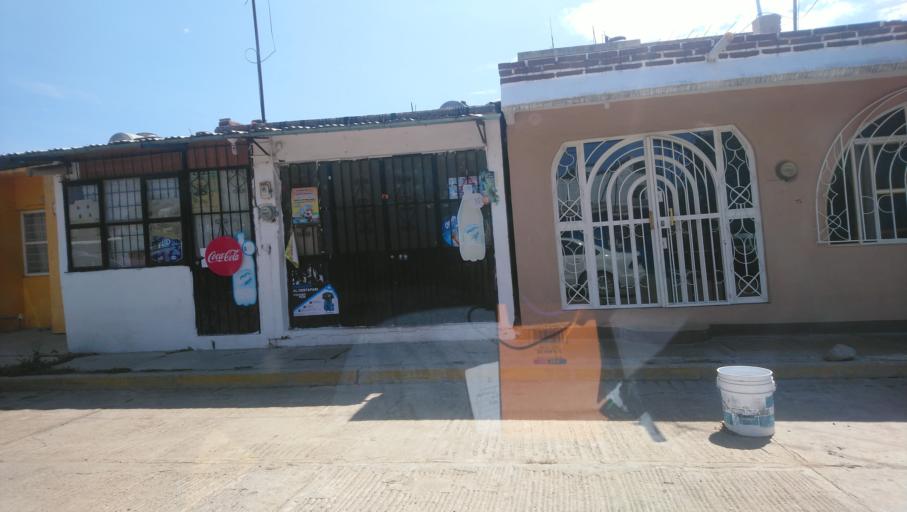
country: MX
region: Oaxaca
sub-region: Santo Domingo Tehuantepec
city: La Noria
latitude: 16.2567
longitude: -95.2212
